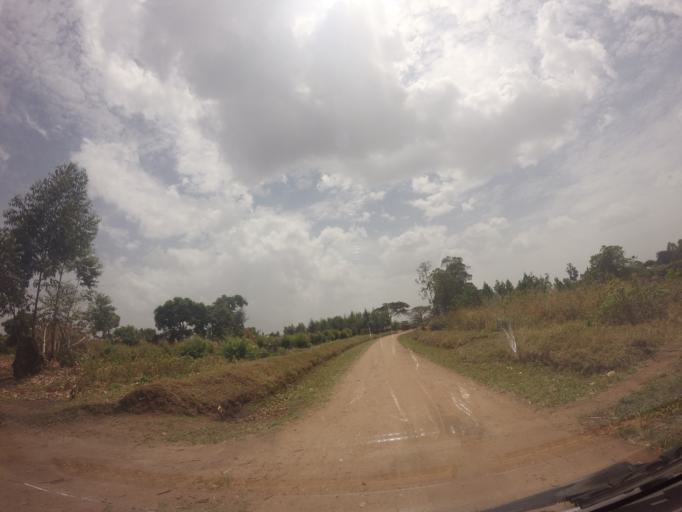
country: UG
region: Northern Region
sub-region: Arua District
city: Arua
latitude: 2.8185
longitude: 30.9001
